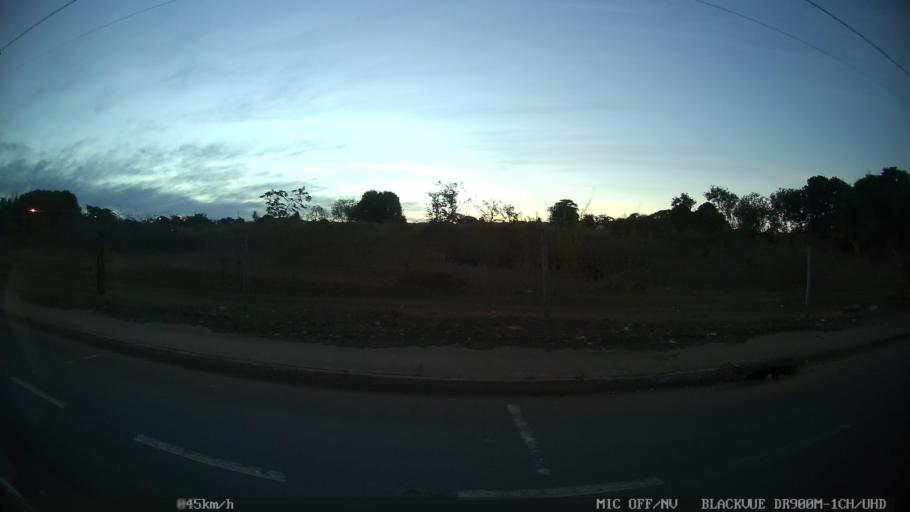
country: BR
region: Sao Paulo
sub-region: Catanduva
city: Catanduva
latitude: -21.1324
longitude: -48.9868
